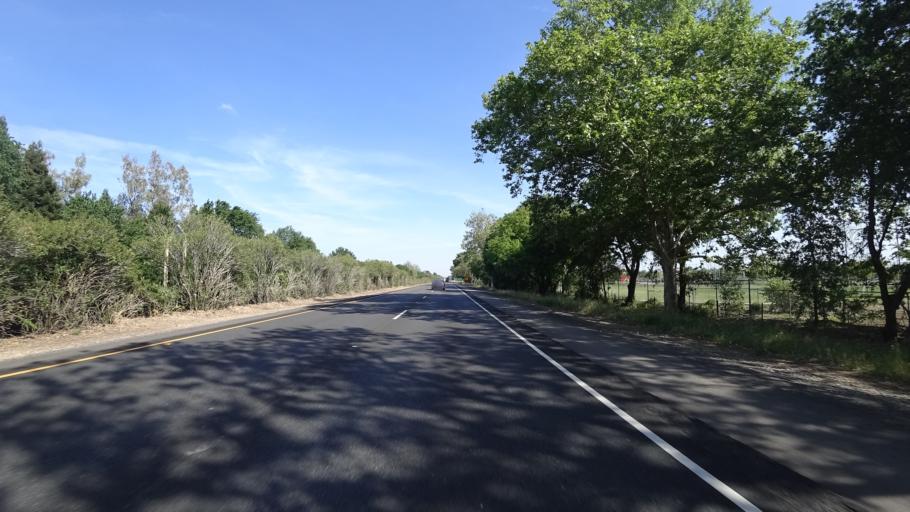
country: US
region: California
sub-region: Butte County
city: Chico
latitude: 39.7805
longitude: -121.8810
